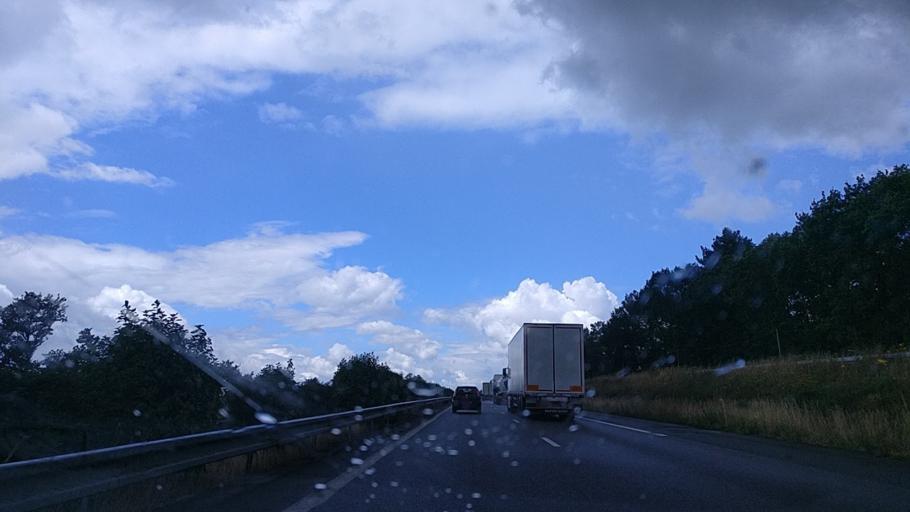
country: FR
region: Brittany
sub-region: Departement du Morbihan
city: Ambon
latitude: 47.5974
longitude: -2.5771
